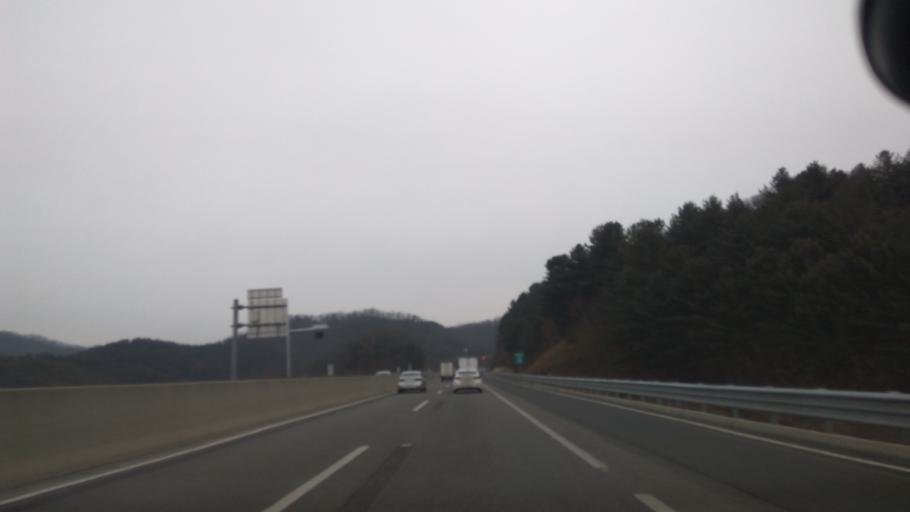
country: KR
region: Gangwon-do
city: Sindong
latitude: 37.7372
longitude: 127.6312
